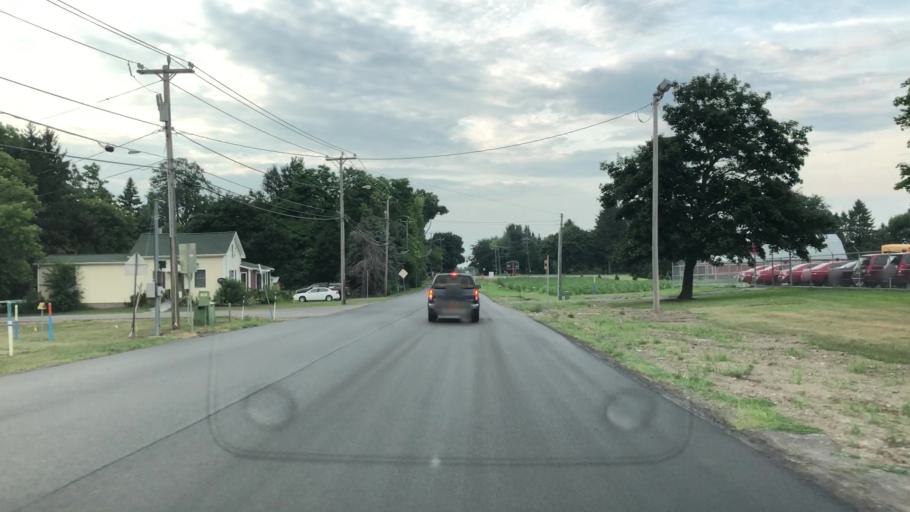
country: US
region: New York
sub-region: Erie County
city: Elma Center
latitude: 42.8371
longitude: -78.6060
